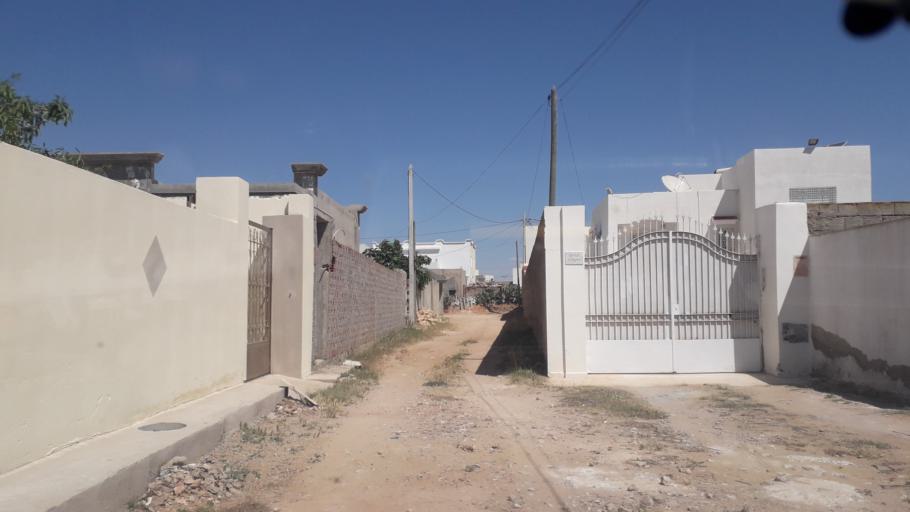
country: TN
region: Safaqis
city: Al Qarmadah
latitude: 34.8308
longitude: 10.7674
